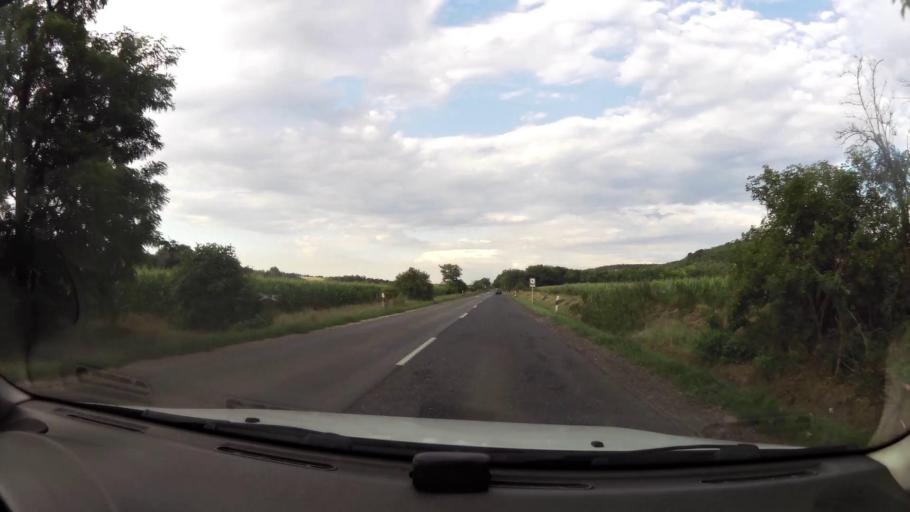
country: HU
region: Pest
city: Mende
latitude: 47.4406
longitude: 19.4844
